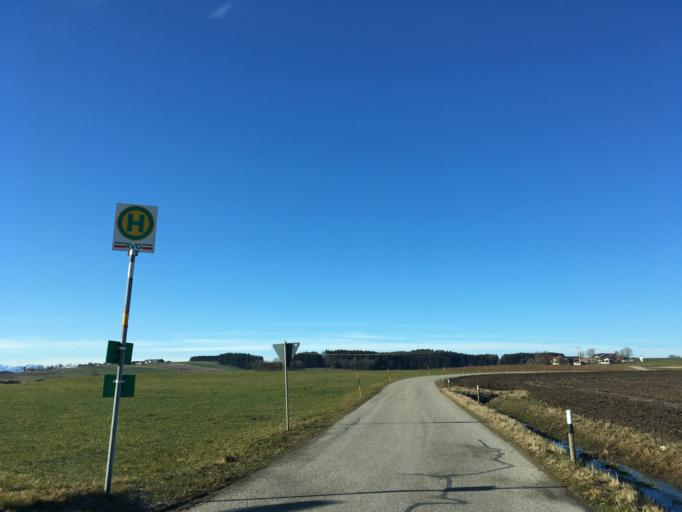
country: DE
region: Bavaria
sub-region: Upper Bavaria
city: Pittenhart
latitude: 47.9921
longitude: 12.3643
